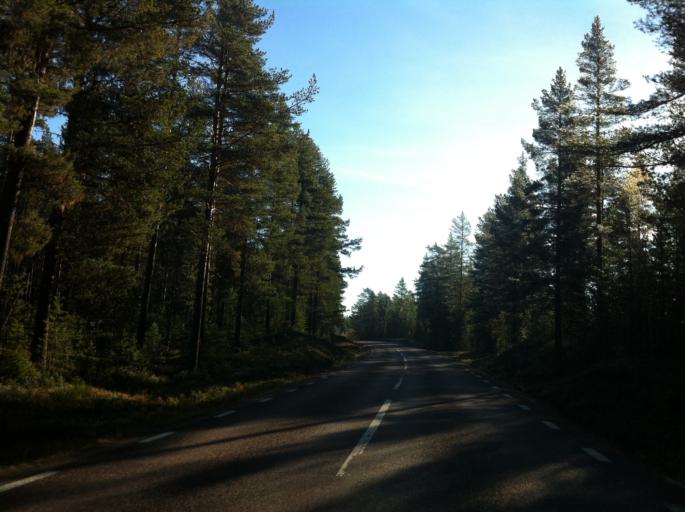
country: NO
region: Hedmark
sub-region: Trysil
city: Innbygda
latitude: 61.8420
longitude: 12.8004
